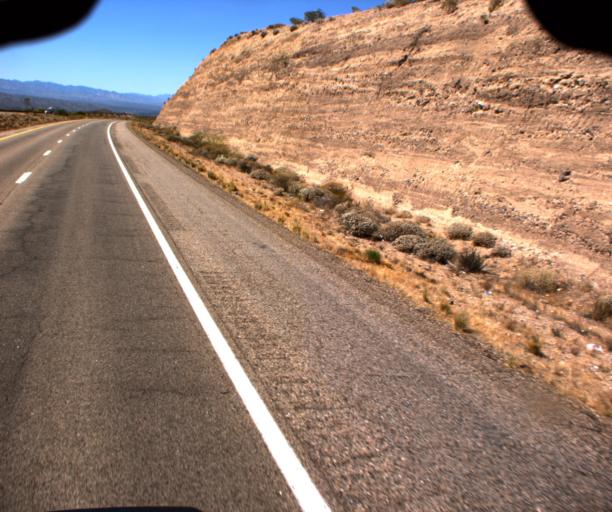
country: US
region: Arizona
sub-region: Yavapai County
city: Bagdad
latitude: 34.5929
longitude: -113.5135
